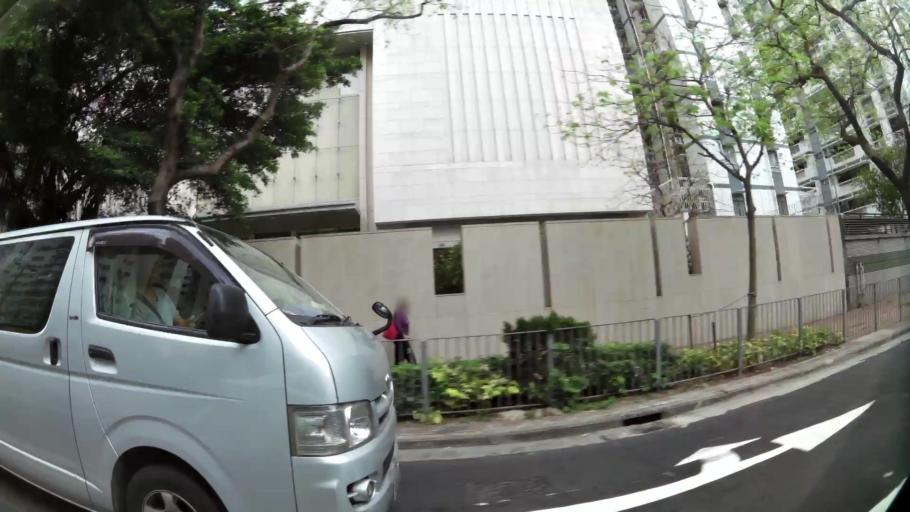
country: HK
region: Kowloon City
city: Kowloon
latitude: 22.3251
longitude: 114.1755
